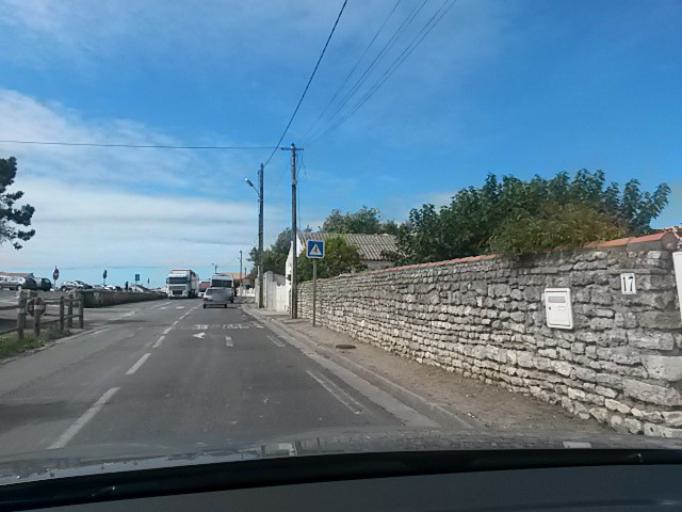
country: FR
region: Poitou-Charentes
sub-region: Departement de la Charente-Maritime
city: Dolus-d'Oleron
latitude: 45.9145
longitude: -1.3239
